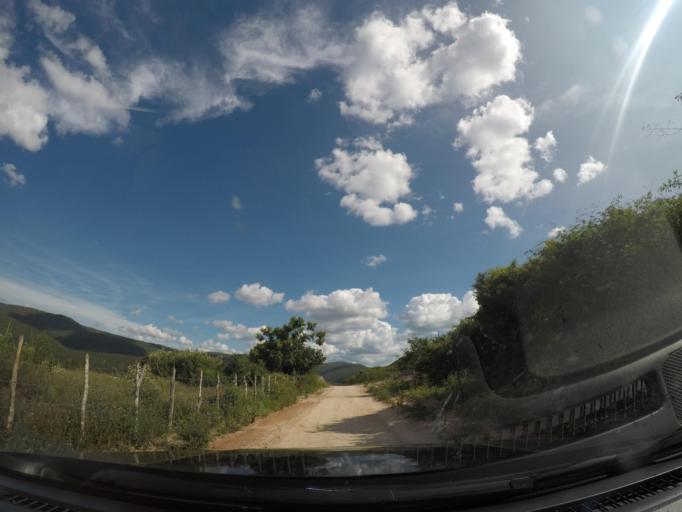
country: BR
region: Bahia
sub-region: Barra Da Estiva
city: Barra da Estiva
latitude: -13.2023
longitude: -41.5944
